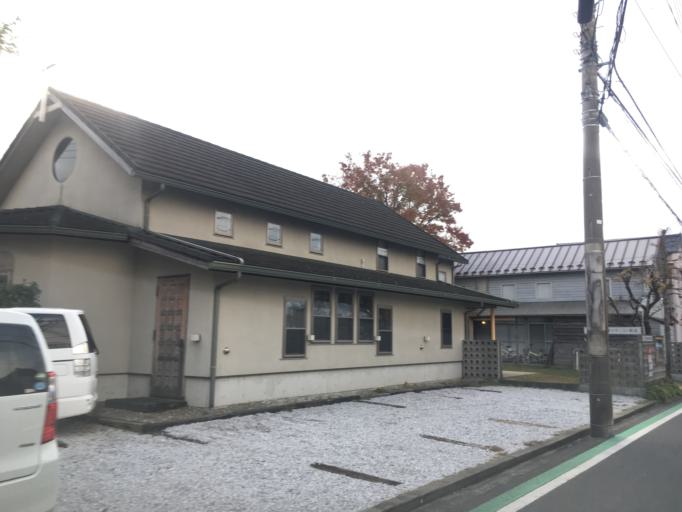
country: JP
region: Tokyo
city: Chofugaoka
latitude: 35.6283
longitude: 139.5878
